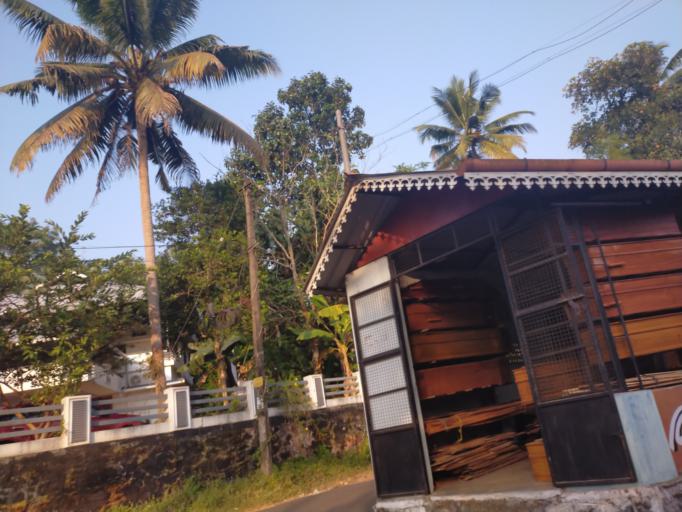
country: IN
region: Kerala
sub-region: Kottayam
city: Vaikam
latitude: 9.7569
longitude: 76.4969
